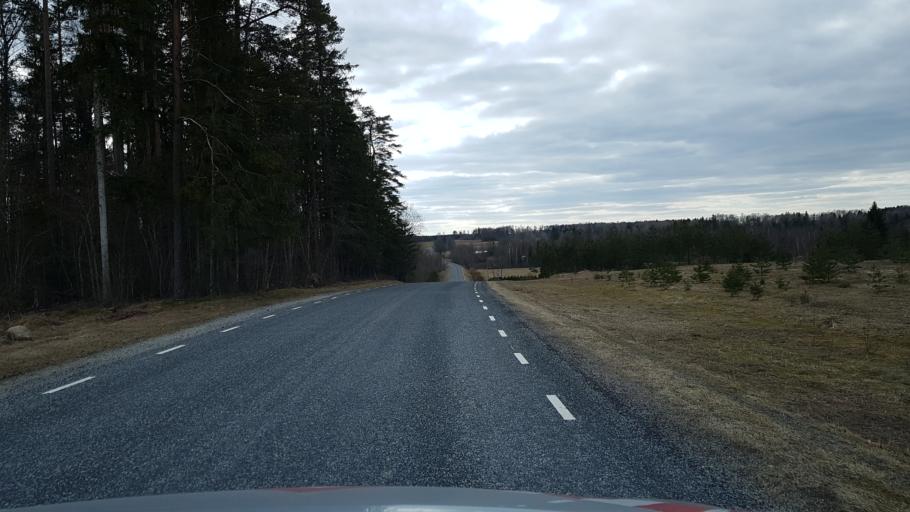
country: EE
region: Laeaene-Virumaa
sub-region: Tamsalu vald
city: Tamsalu
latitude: 59.2125
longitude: 26.1534
